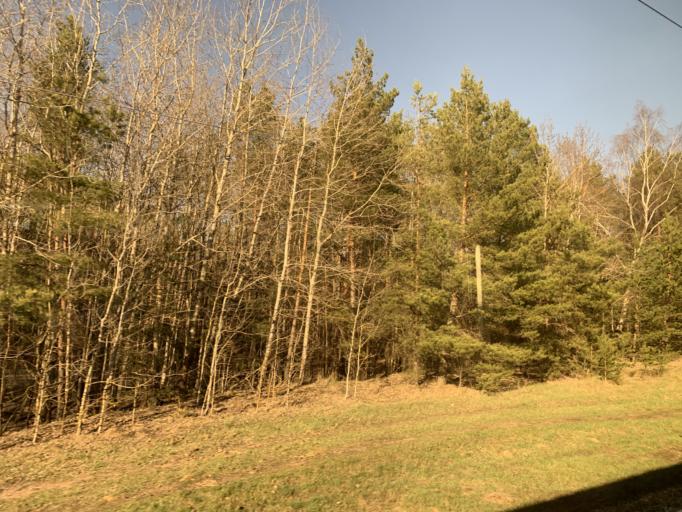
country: BY
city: Soly
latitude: 54.4930
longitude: 26.2847
